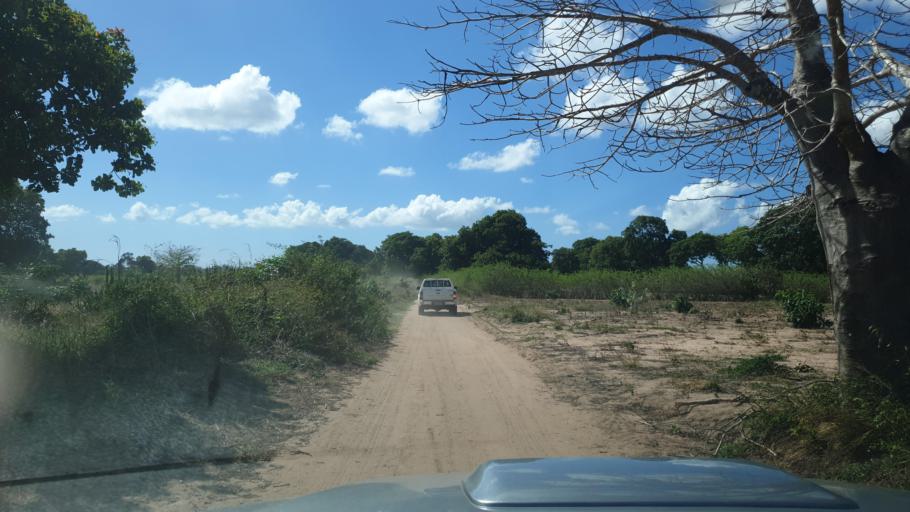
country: MZ
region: Nampula
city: Nacala
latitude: -14.4702
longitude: 40.6962
